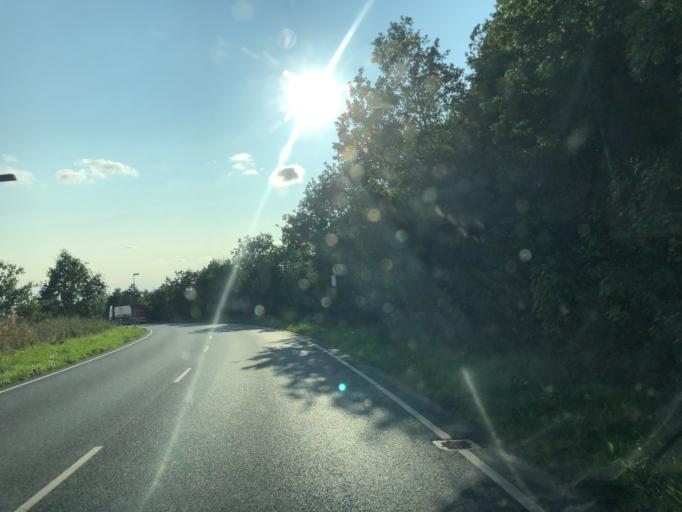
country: DK
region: Central Jutland
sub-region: Viborg Kommune
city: Viborg
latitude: 56.4602
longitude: 9.3640
